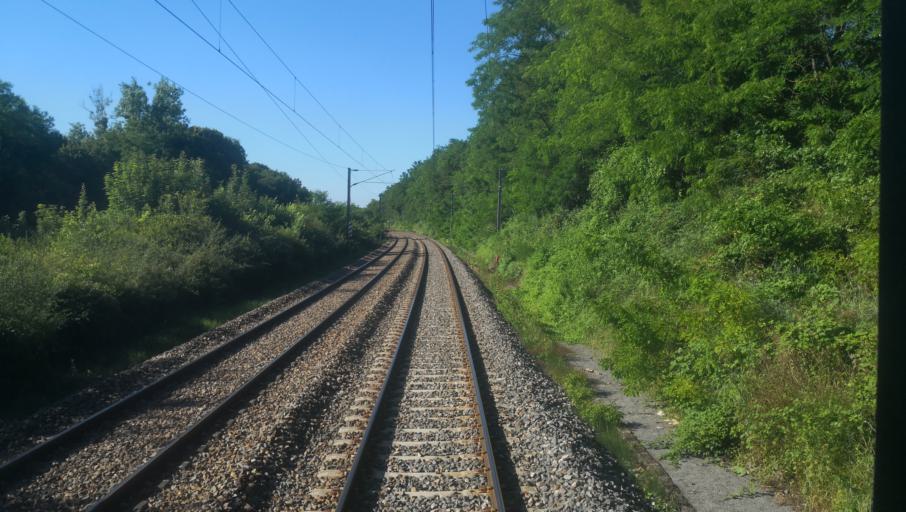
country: FR
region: Bourgogne
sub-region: Departement de la Nievre
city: Cosne-Cours-sur-Loire
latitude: 47.4350
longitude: 2.9337
